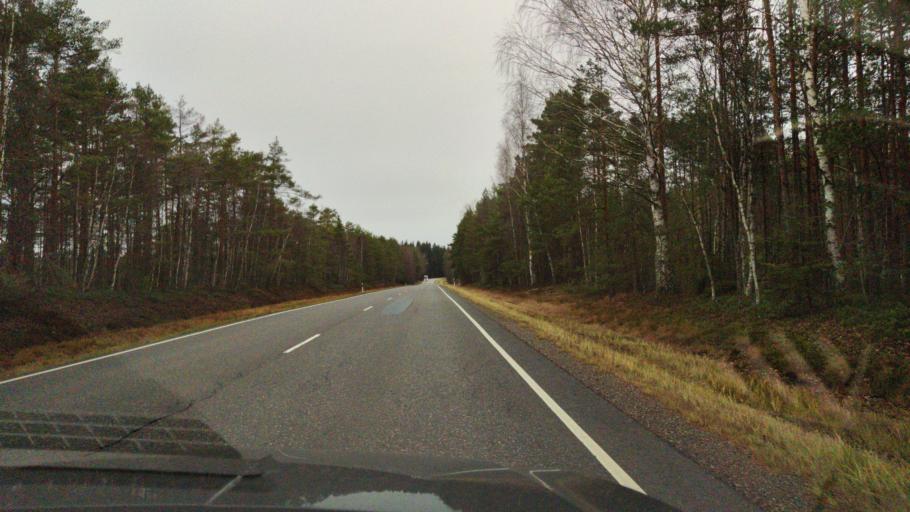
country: FI
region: Varsinais-Suomi
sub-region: Loimaa
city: Ylaene
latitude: 60.7490
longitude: 22.4269
